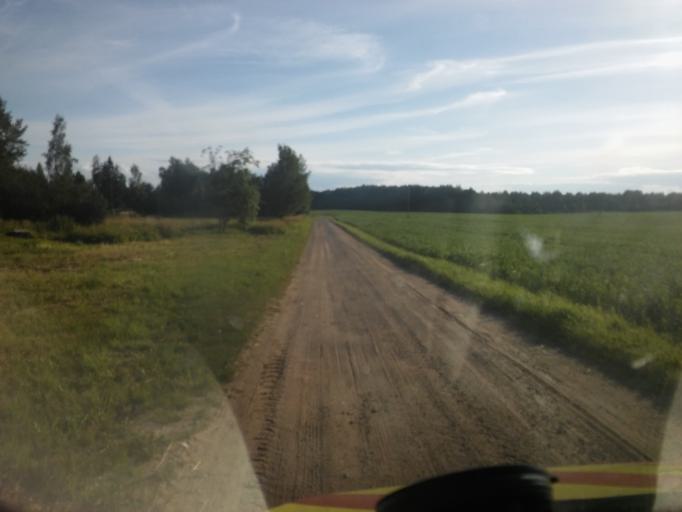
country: EE
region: Valgamaa
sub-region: Torva linn
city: Torva
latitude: 58.1048
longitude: 26.0074
